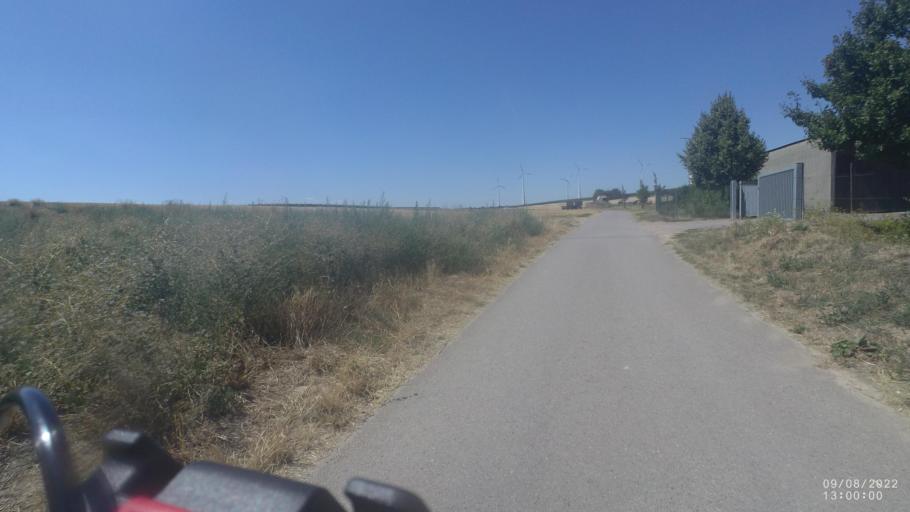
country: DE
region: Rheinland-Pfalz
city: Gabsheim
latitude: 49.8272
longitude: 8.1641
